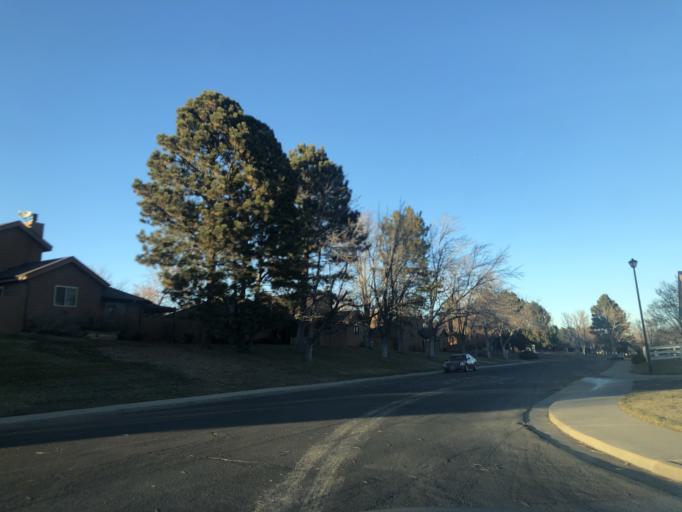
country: US
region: Colorado
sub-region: Adams County
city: Aurora
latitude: 39.7140
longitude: -104.8152
